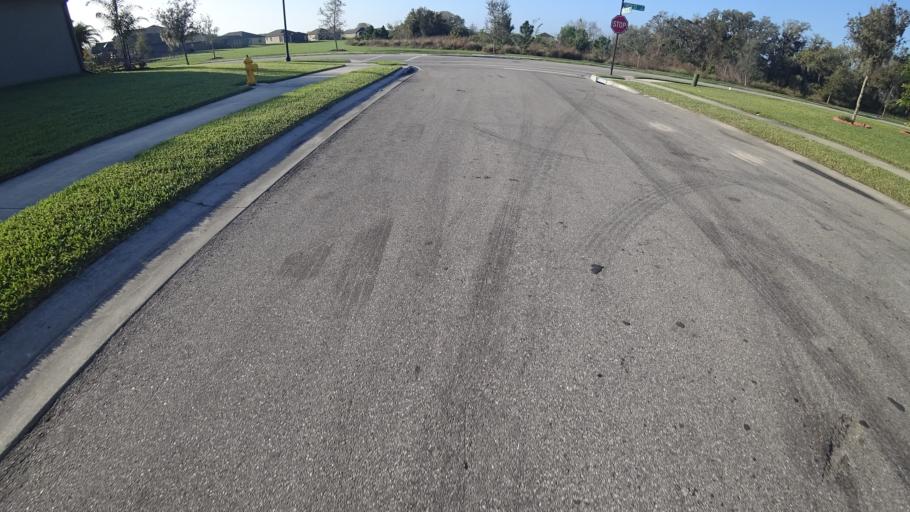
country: US
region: Florida
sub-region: Manatee County
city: Ellenton
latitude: 27.5689
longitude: -82.4518
